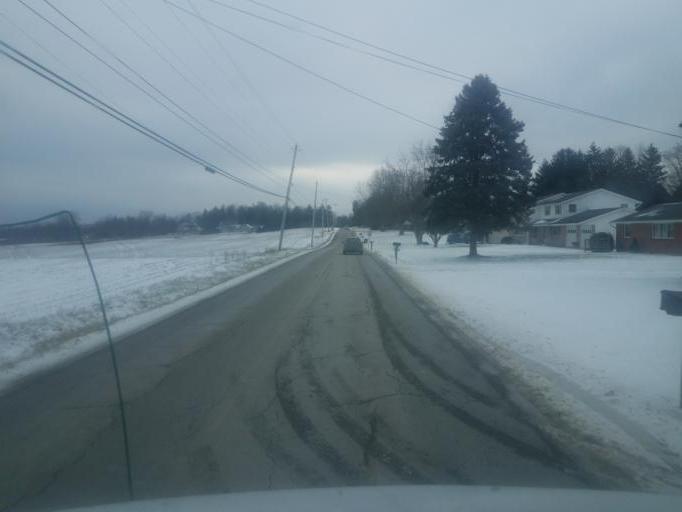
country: US
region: Ohio
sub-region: Richland County
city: Ontario
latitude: 40.7217
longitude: -82.5597
